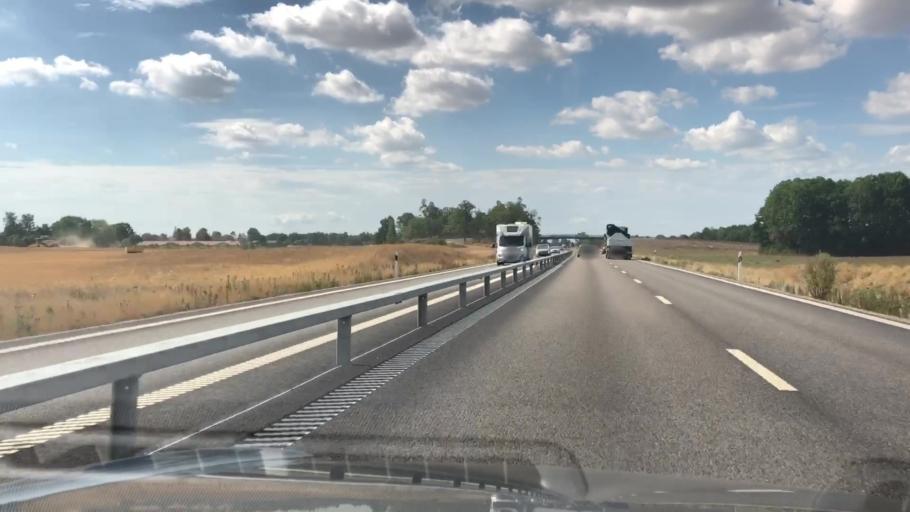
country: SE
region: Kalmar
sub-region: Kalmar Kommun
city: Rinkabyholm
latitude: 56.6584
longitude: 16.2510
